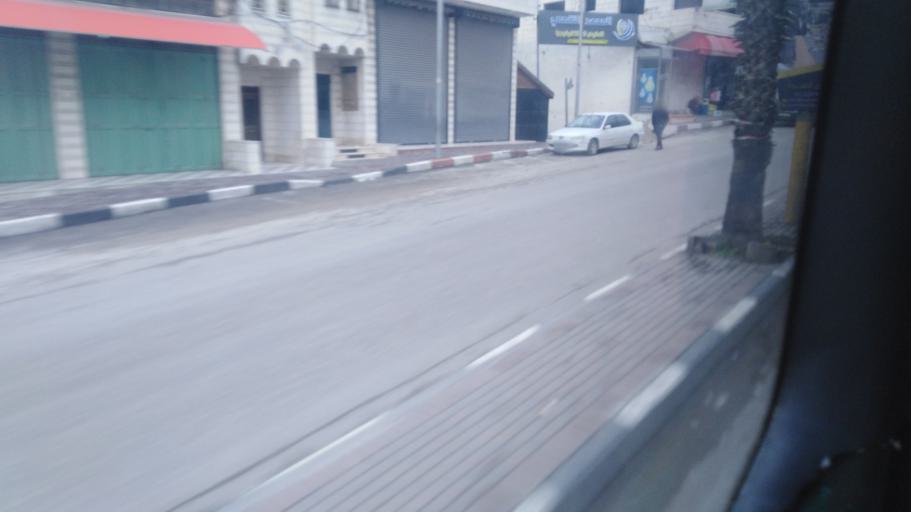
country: PS
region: West Bank
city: Hebron
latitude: 31.5297
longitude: 35.0891
